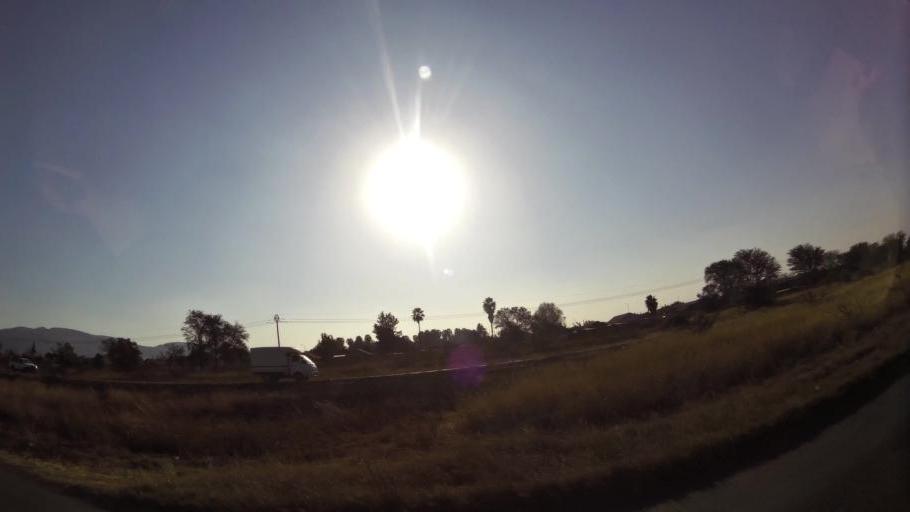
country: ZA
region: North-West
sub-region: Bojanala Platinum District Municipality
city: Rustenburg
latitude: -25.6455
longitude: 27.2283
